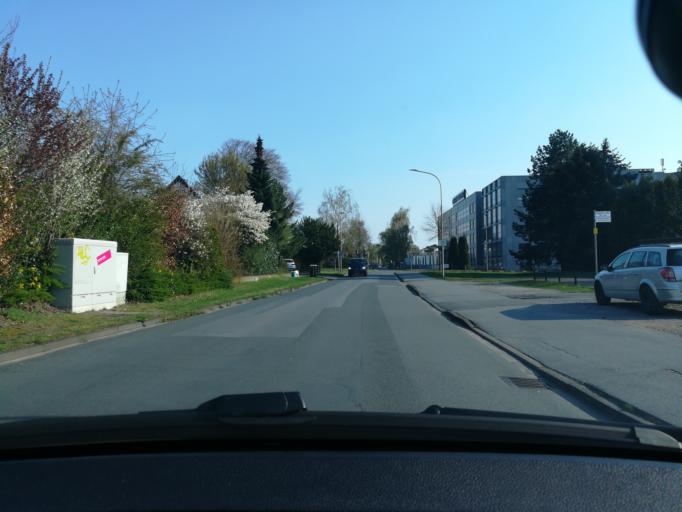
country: DE
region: North Rhine-Westphalia
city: Halle
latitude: 52.0490
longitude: 8.3746
